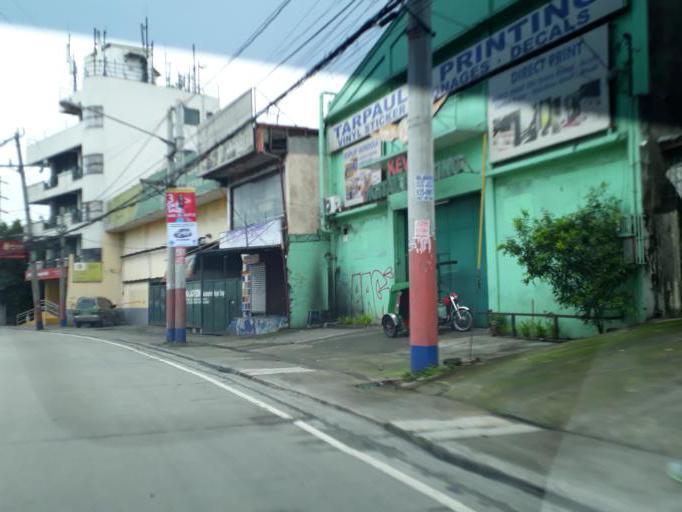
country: PH
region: Metro Manila
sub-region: Caloocan City
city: Niugan
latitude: 14.6651
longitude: 120.9844
